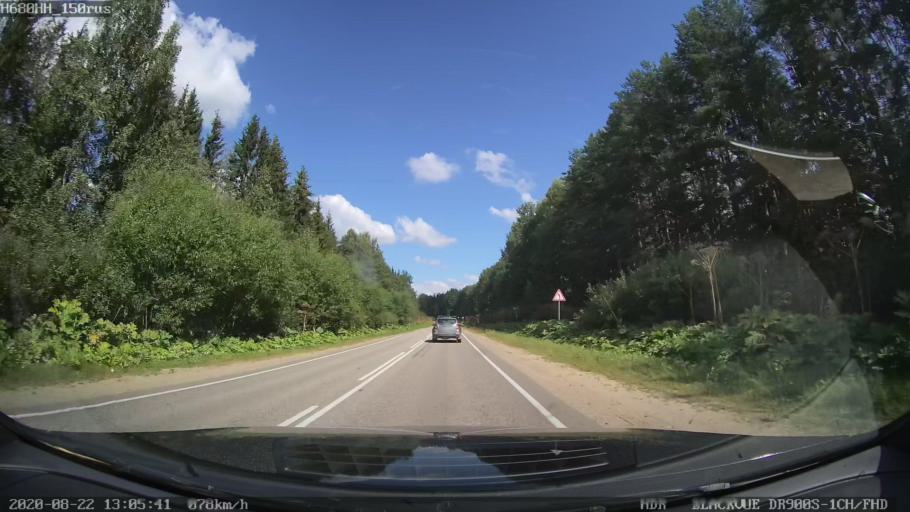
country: RU
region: Tverskaya
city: Bezhetsk
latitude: 57.6743
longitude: 36.4509
